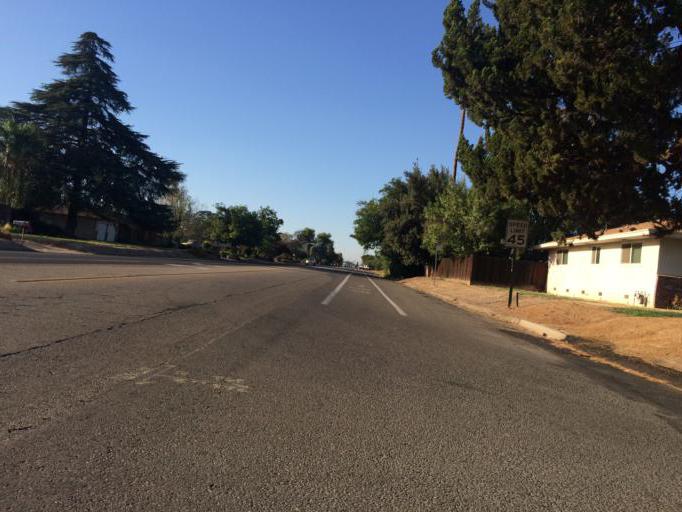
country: US
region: California
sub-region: Fresno County
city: Sunnyside
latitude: 36.7304
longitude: -119.6821
